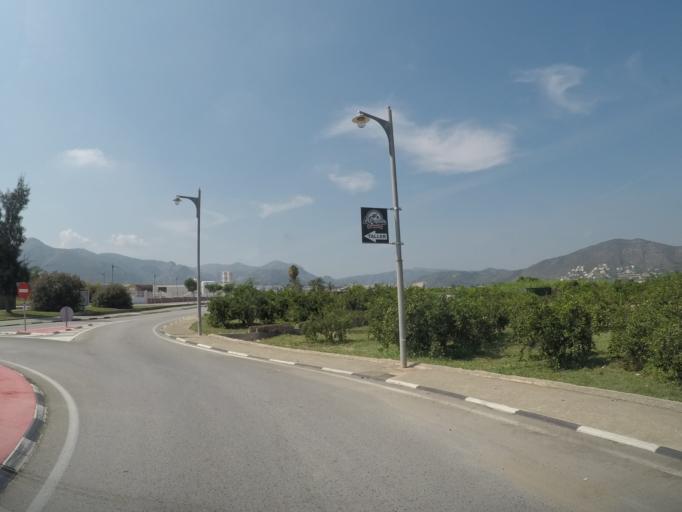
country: ES
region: Valencia
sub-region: Provincia de Alicante
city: Pego
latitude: 38.8458
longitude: -0.0956
